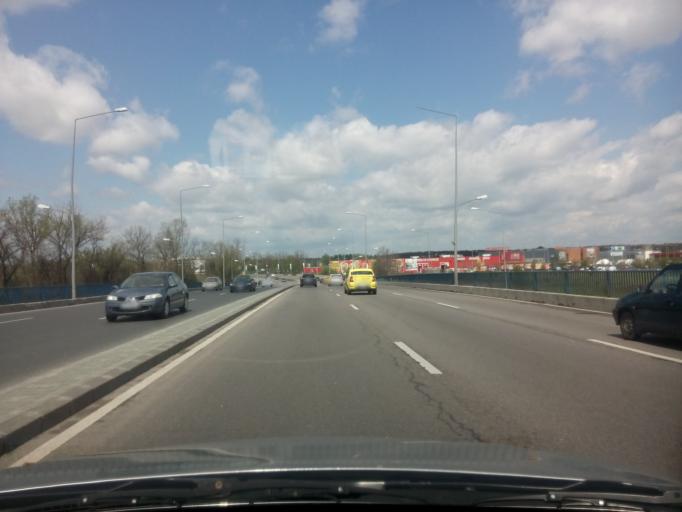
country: RO
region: Ilfov
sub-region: Comuna Otopeni
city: Otopeni
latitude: 44.5059
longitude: 26.0819
